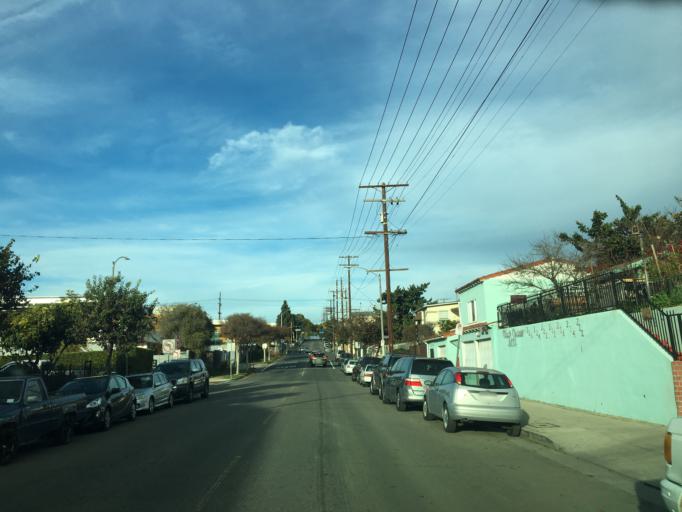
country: US
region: California
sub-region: Los Angeles County
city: Silver Lake
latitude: 34.0717
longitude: -118.2765
